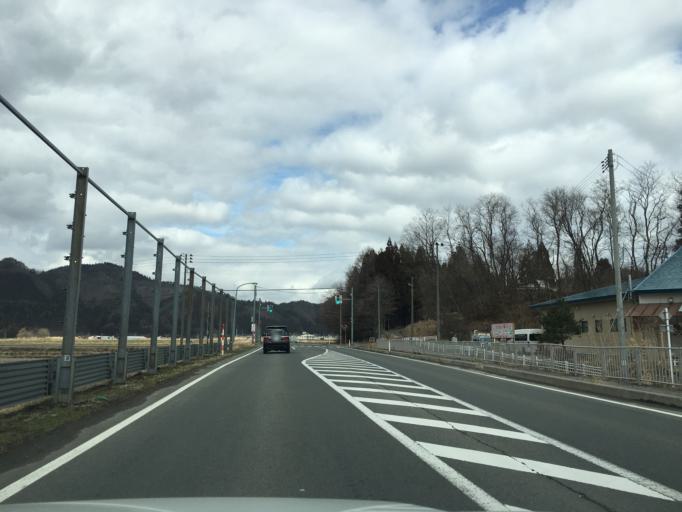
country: JP
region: Akita
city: Hanawa
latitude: 40.2355
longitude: 140.7356
